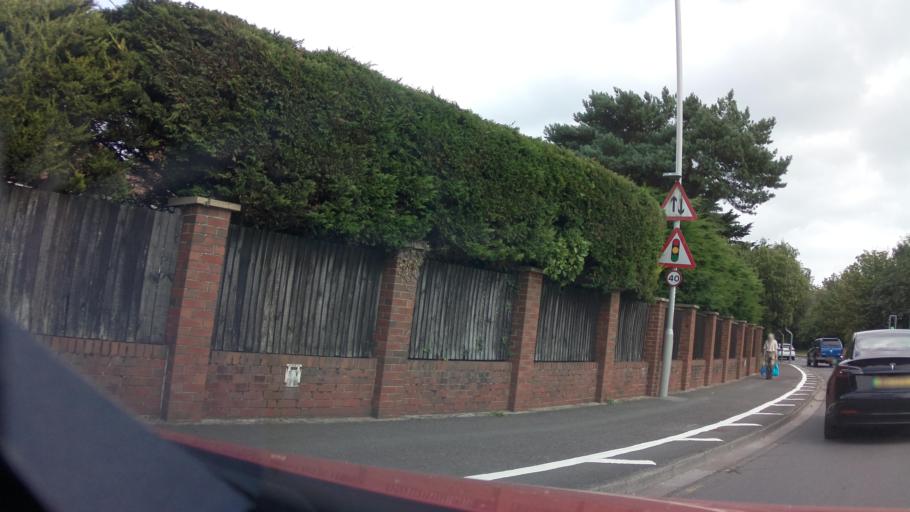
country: GB
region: England
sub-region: Hampshire
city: Bransgore
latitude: 50.7410
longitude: -1.7327
